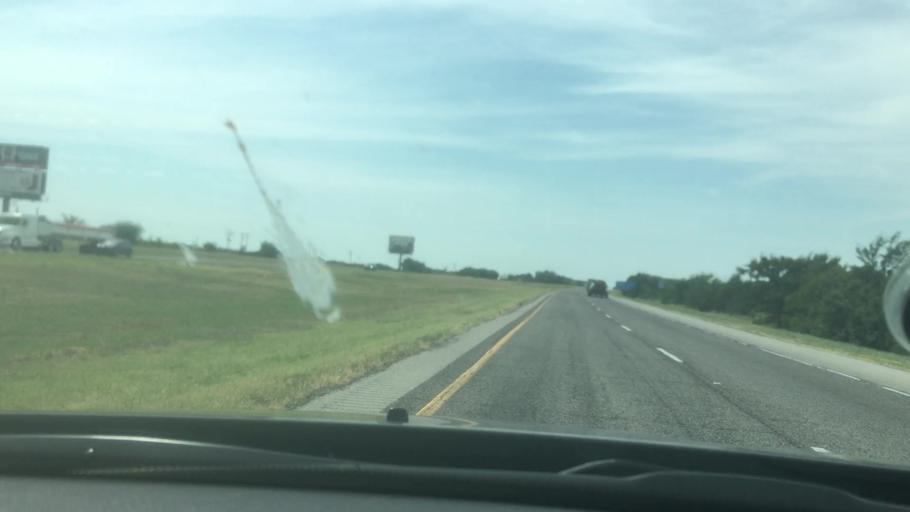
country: US
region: Oklahoma
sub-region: Garvin County
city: Wynnewood
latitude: 34.5652
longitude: -97.1962
